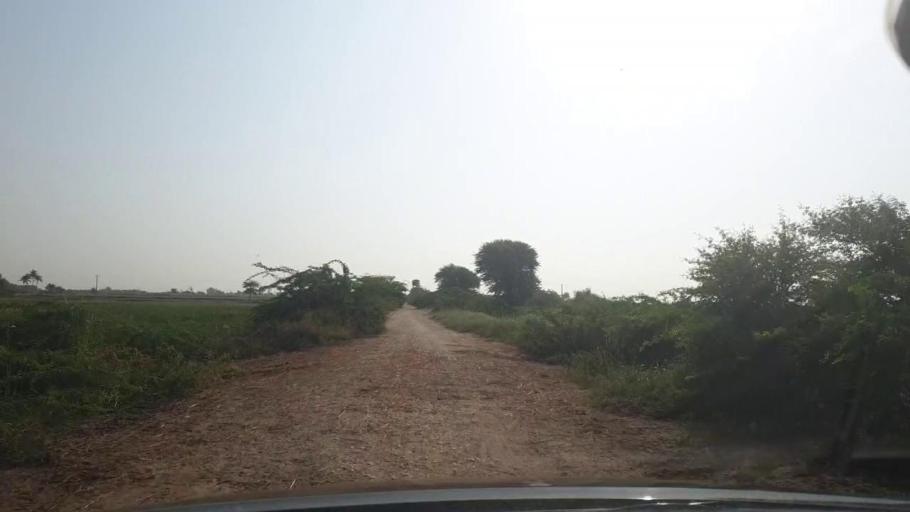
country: PK
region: Sindh
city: Tando Bago
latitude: 24.6509
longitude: 69.1606
